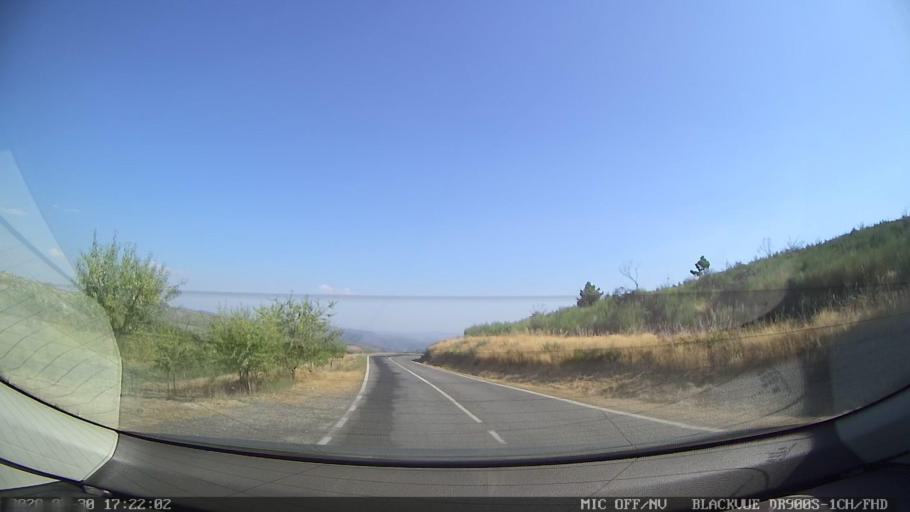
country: PT
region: Vila Real
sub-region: Sabrosa
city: Sabrosa
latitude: 41.3018
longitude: -7.4772
